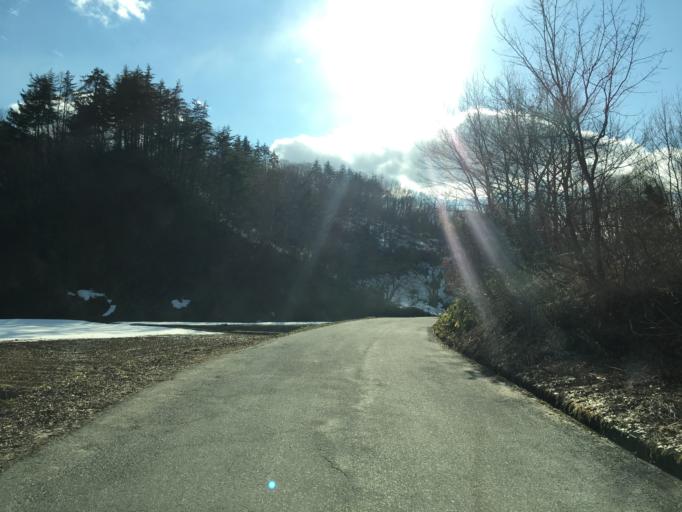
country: JP
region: Yamagata
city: Yonezawa
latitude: 37.9298
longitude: 139.9592
